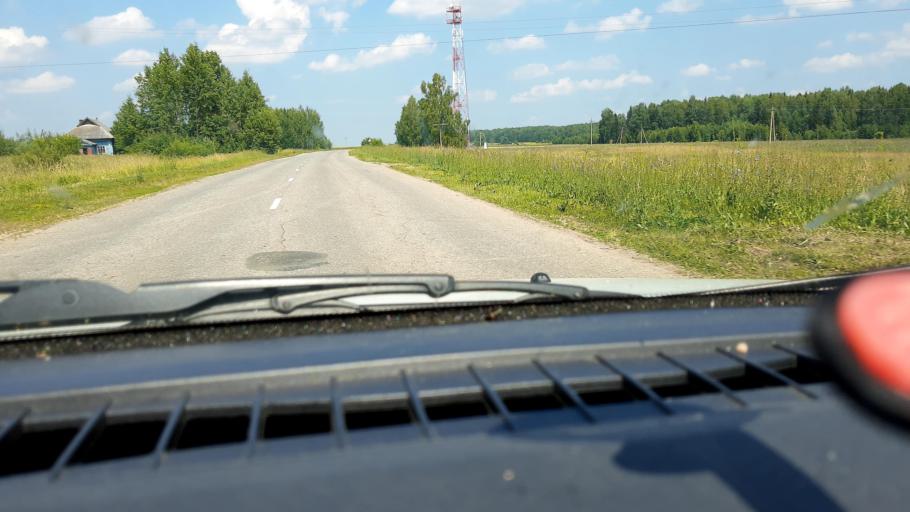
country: RU
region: Nizjnij Novgorod
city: Sharanga
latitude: 57.0556
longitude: 46.5455
